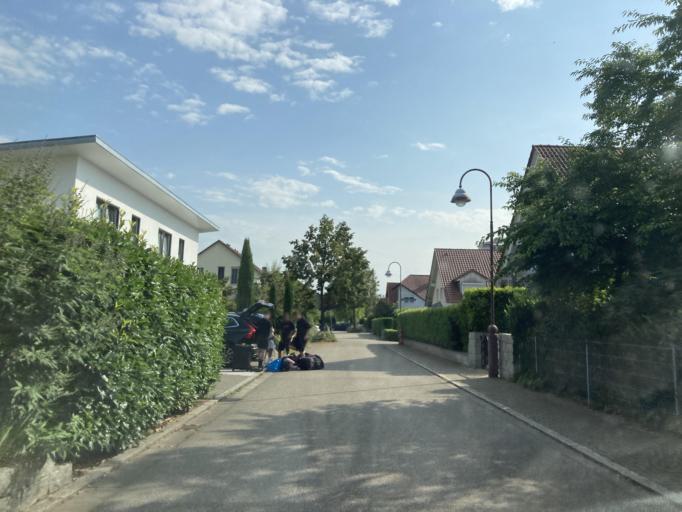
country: DE
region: Baden-Wuerttemberg
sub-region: Freiburg Region
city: Neuenburg am Rhein
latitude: 47.8172
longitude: 7.5721
